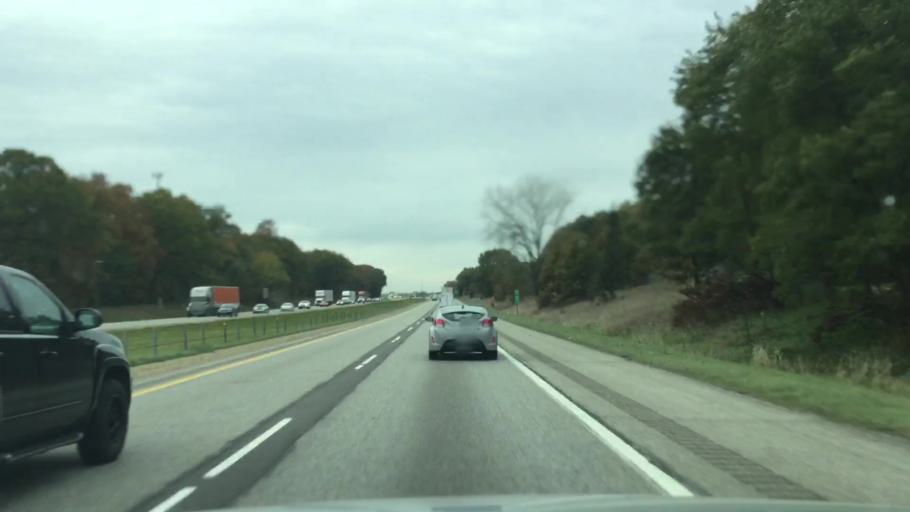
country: US
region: Michigan
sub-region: Kalamazoo County
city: Galesburg
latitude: 42.2825
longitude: -85.3606
